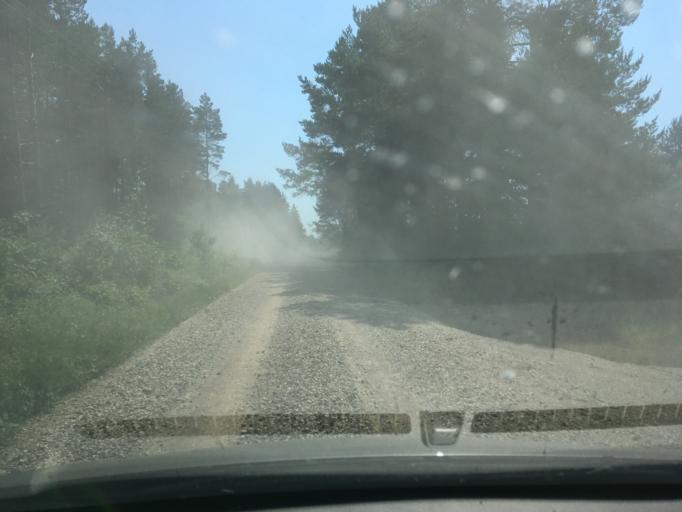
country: EE
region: Laeaene
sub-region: Lihula vald
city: Lihula
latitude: 58.5881
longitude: 23.7148
